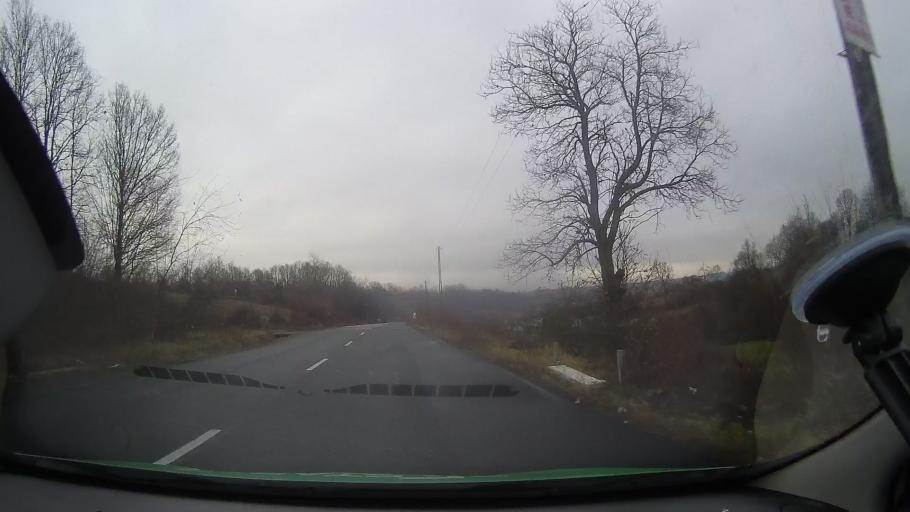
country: RO
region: Arad
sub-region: Comuna Varfurile
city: Varfurile
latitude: 46.3215
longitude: 22.4999
